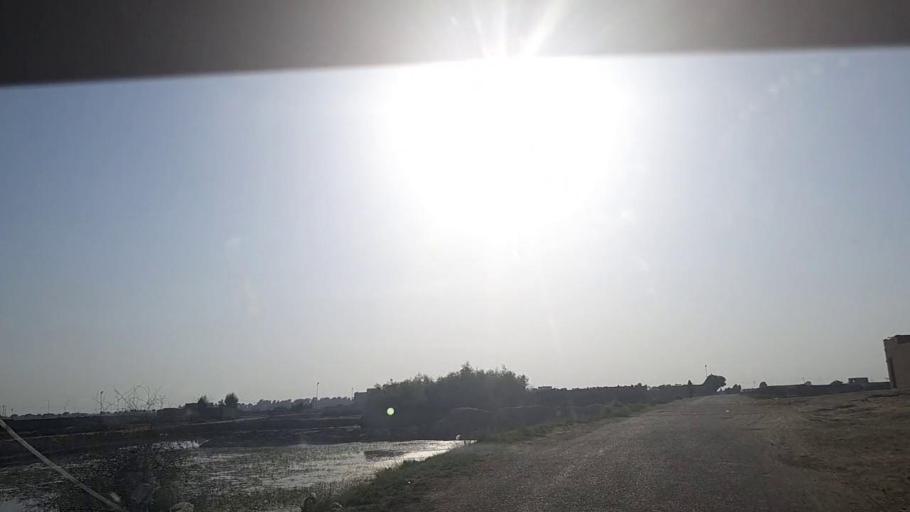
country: PK
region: Sindh
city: Tangwani
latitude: 28.2613
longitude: 69.0072
